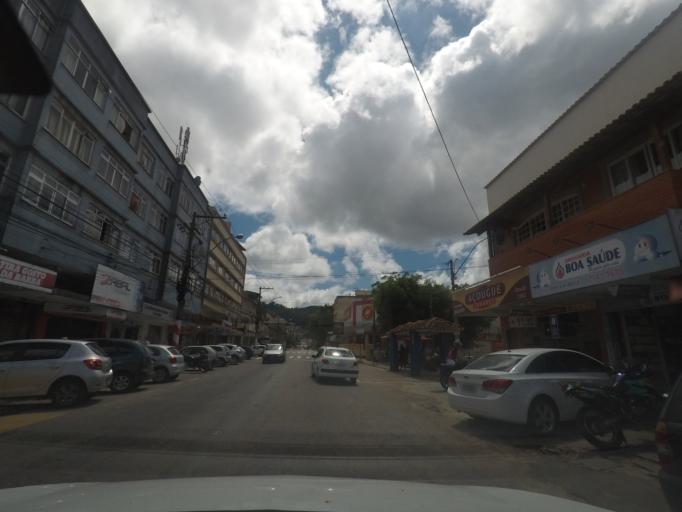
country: BR
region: Rio de Janeiro
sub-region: Teresopolis
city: Teresopolis
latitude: -22.4009
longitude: -42.9782
